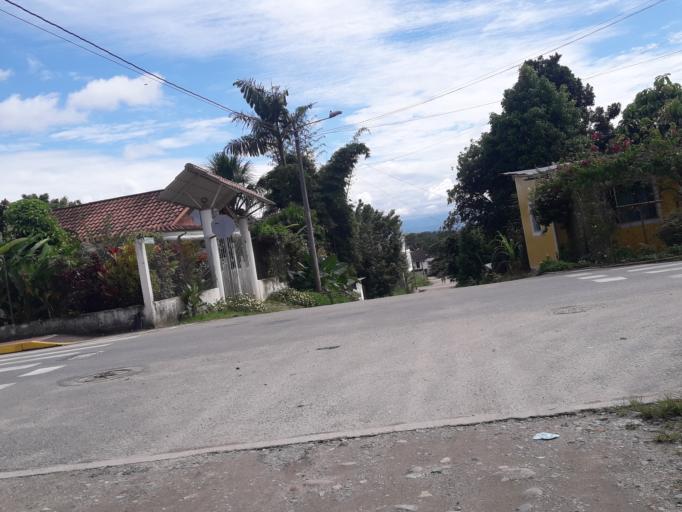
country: EC
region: Napo
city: Tena
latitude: -1.0061
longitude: -77.8163
